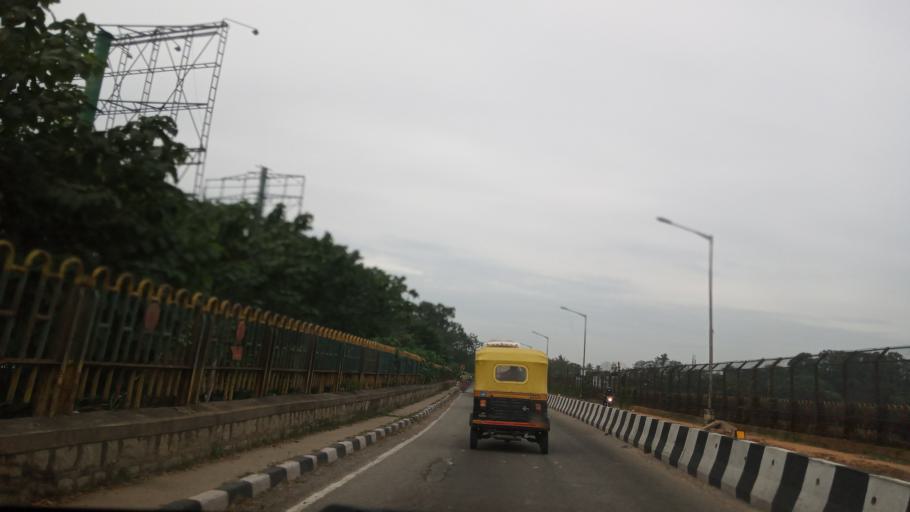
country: IN
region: Karnataka
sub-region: Bangalore Urban
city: Bangalore
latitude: 13.0074
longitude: 77.5755
